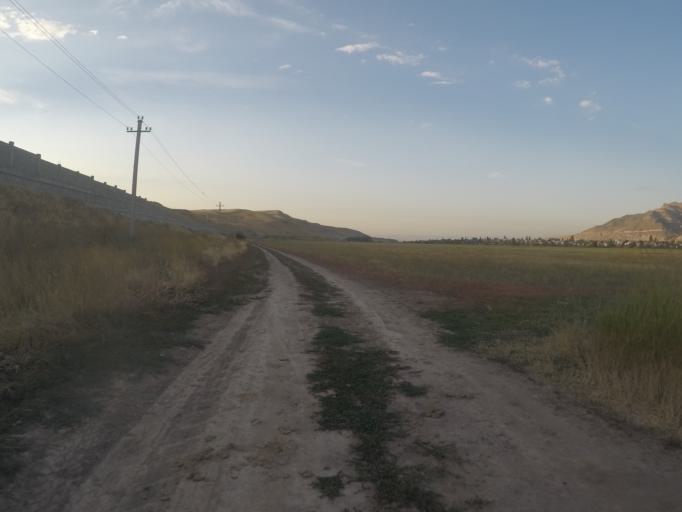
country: KG
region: Chuy
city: Bishkek
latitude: 42.7540
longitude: 74.6366
